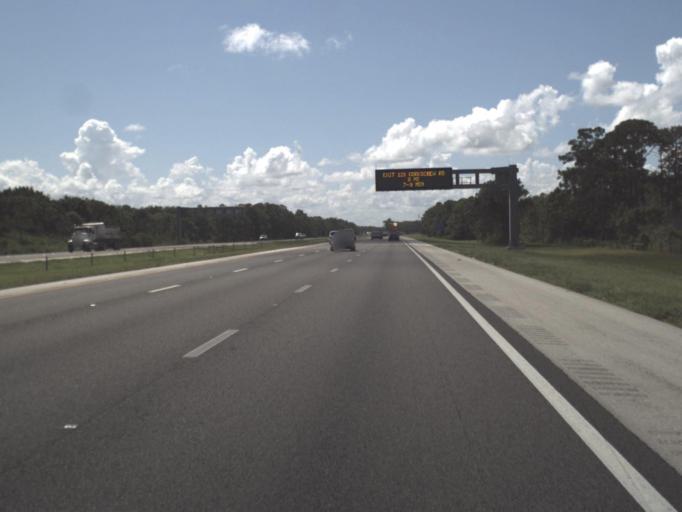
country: US
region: Florida
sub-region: Lee County
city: Gateway
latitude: 26.5910
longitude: -81.7970
